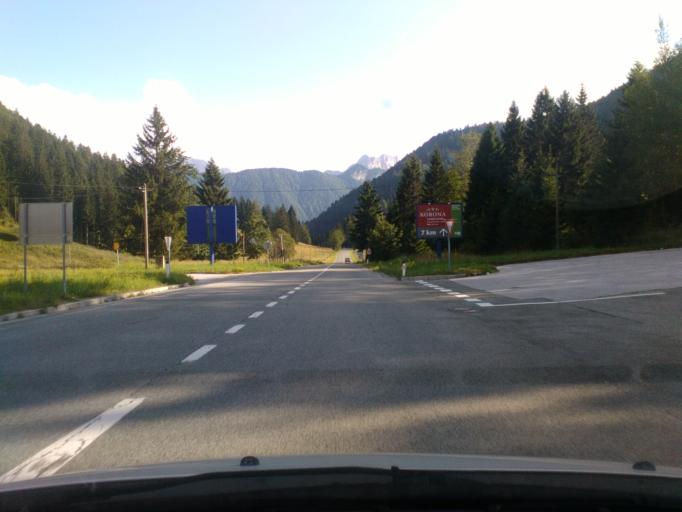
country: AT
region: Carinthia
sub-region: Politischer Bezirk Villach Land
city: Arnoldstein
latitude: 46.5164
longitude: 13.7513
